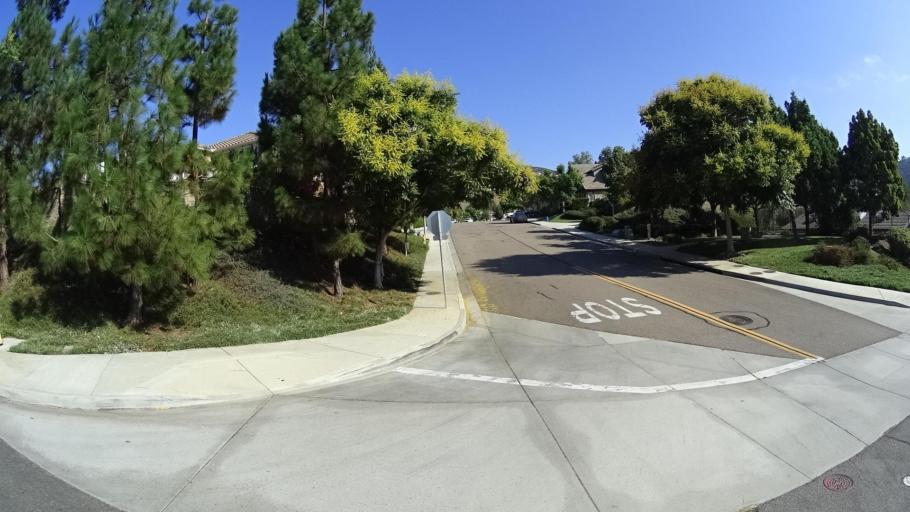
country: US
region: California
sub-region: San Diego County
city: Lake San Marcos
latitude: 33.0958
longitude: -117.1795
